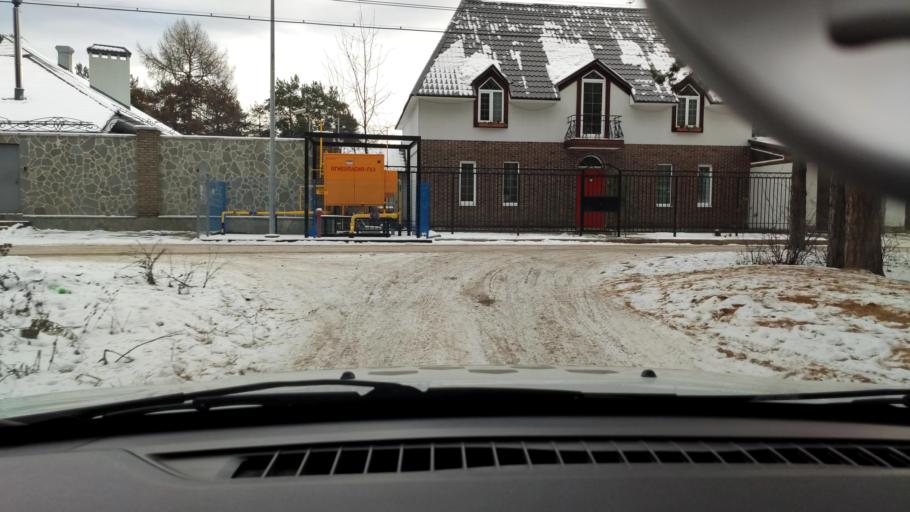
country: RU
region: Perm
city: Perm
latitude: 58.0534
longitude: 56.2857
